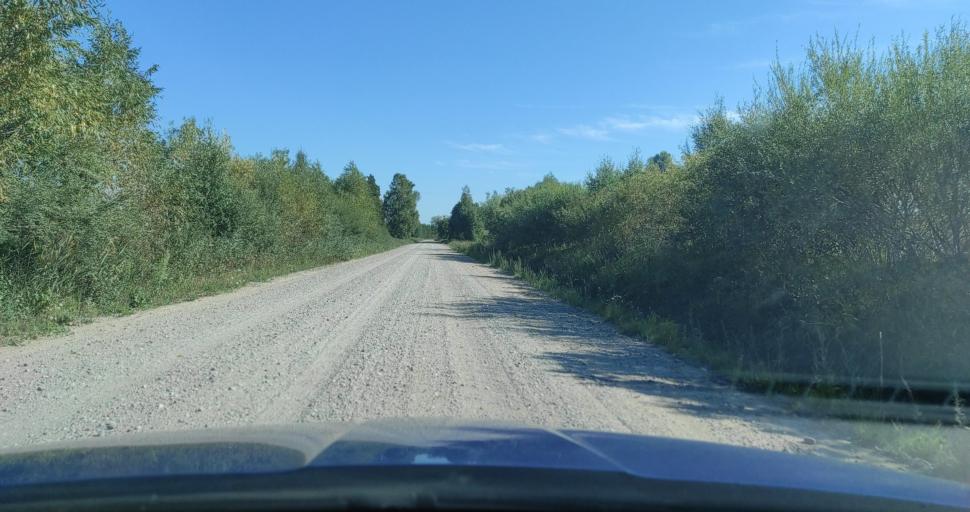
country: LV
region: Pavilostas
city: Pavilosta
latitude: 56.8512
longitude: 21.2707
